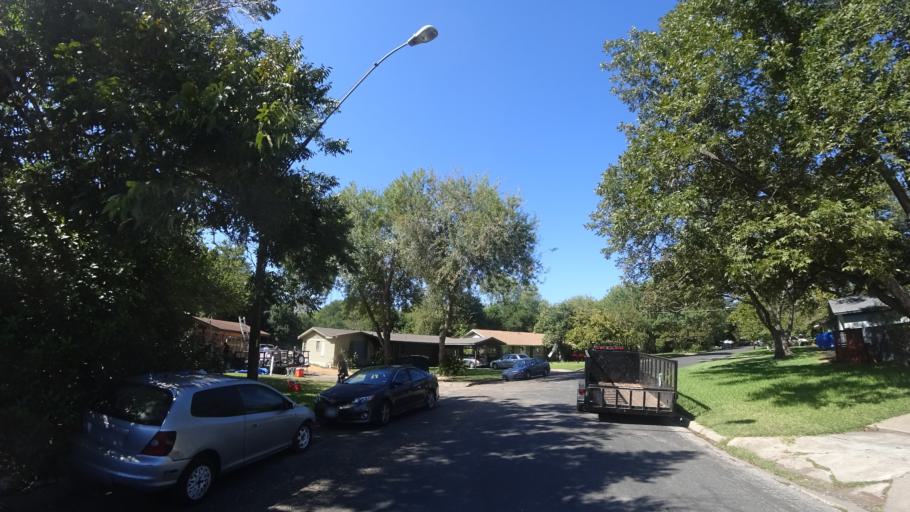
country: US
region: Texas
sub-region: Travis County
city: Austin
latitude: 30.3163
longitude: -97.6948
